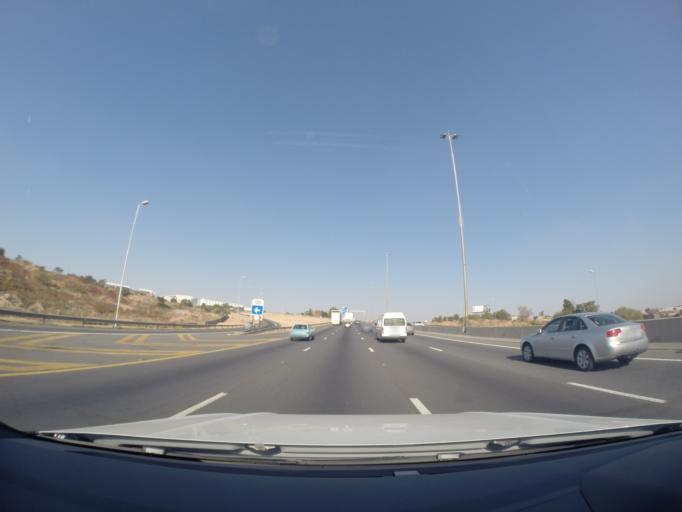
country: ZA
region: Gauteng
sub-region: City of Johannesburg Metropolitan Municipality
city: Modderfontein
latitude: -26.0808
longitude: 28.1169
